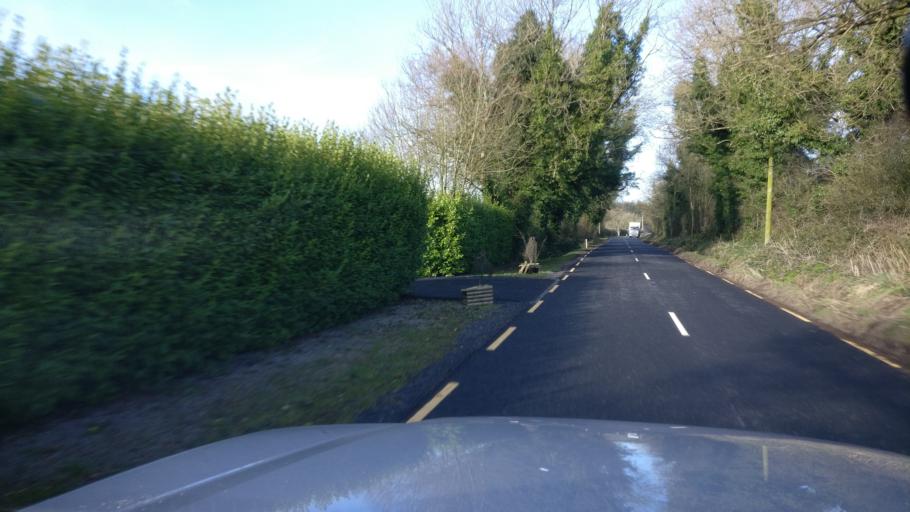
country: IE
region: Leinster
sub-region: Kilkenny
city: Castlecomer
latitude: 52.9071
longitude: -7.1828
